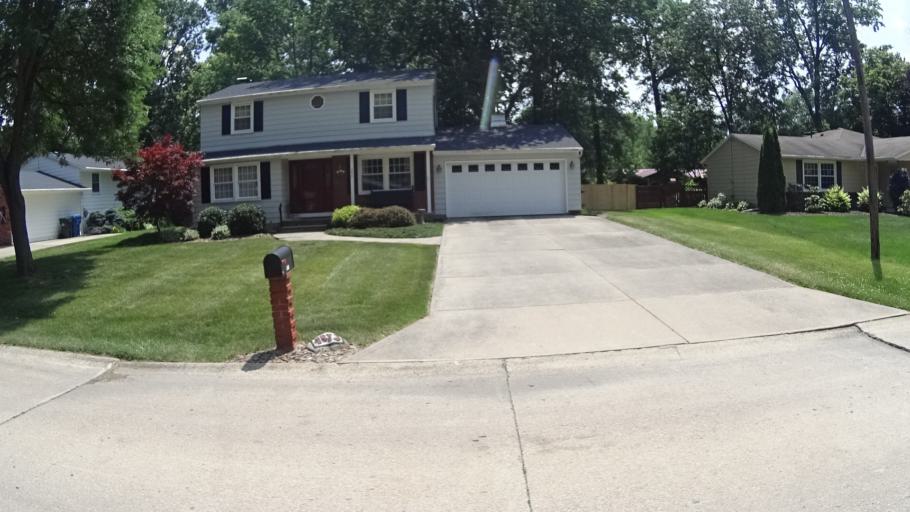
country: US
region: Ohio
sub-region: Lorain County
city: Vermilion
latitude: 41.4079
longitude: -82.3522
